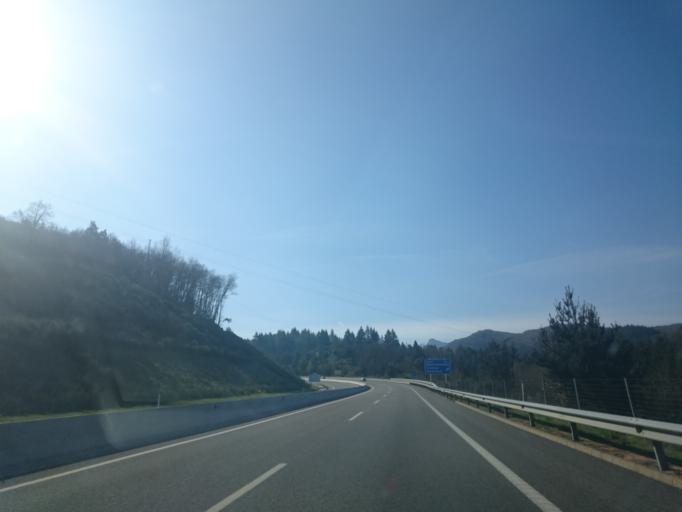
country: ES
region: Catalonia
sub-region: Provincia de Girona
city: Viladrau
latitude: 41.8582
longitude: 2.4242
